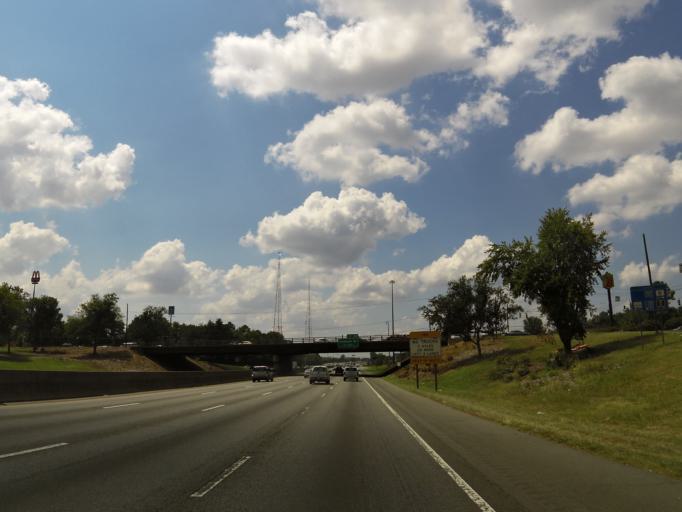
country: US
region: North Carolina
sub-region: Mecklenburg County
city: Charlotte
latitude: 35.2793
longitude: -80.7923
